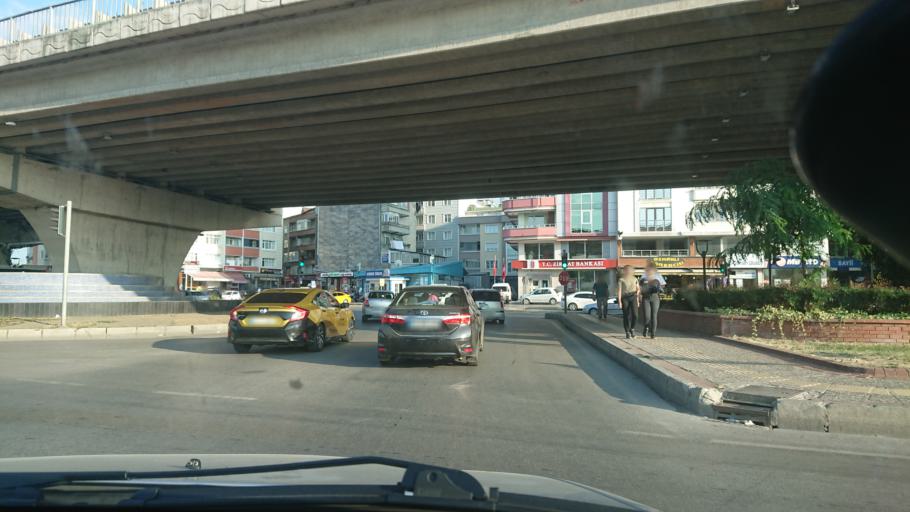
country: TR
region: Samsun
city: Samsun
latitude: 41.2725
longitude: 36.3656
